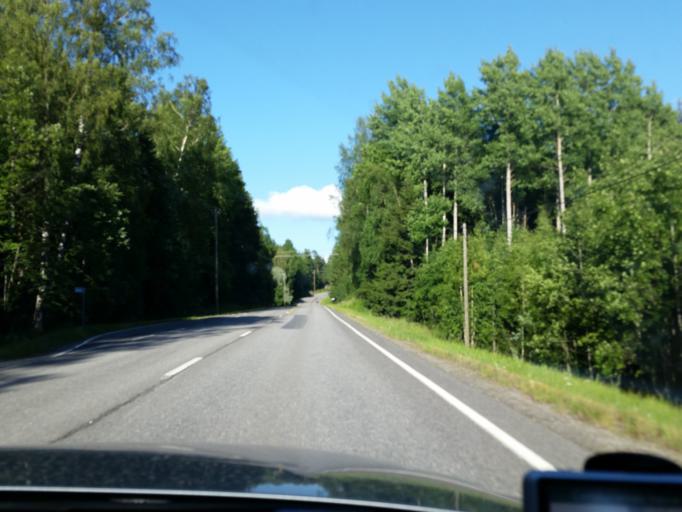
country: FI
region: Uusimaa
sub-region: Helsinki
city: Vihti
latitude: 60.3051
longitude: 24.3004
